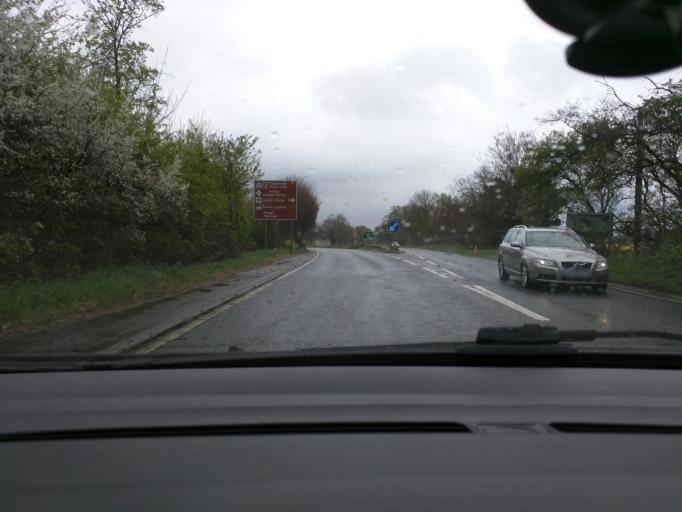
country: GB
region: England
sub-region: Suffolk
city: Saxmundham
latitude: 52.1918
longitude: 1.4644
